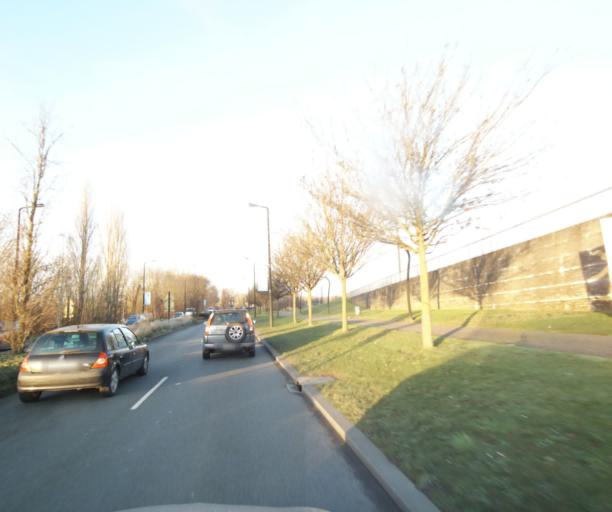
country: FR
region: Nord-Pas-de-Calais
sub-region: Departement du Nord
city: Valenciennes
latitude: 50.3445
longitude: 3.5164
